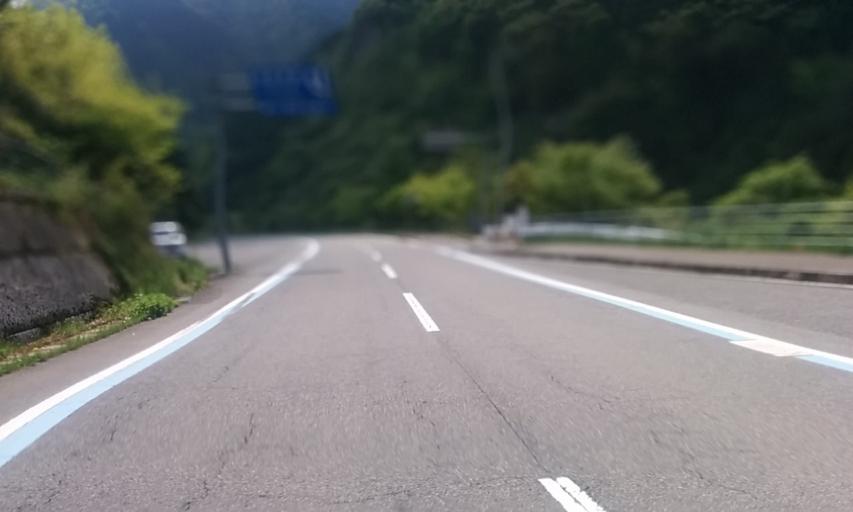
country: JP
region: Ehime
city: Saijo
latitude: 33.8199
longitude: 133.2333
